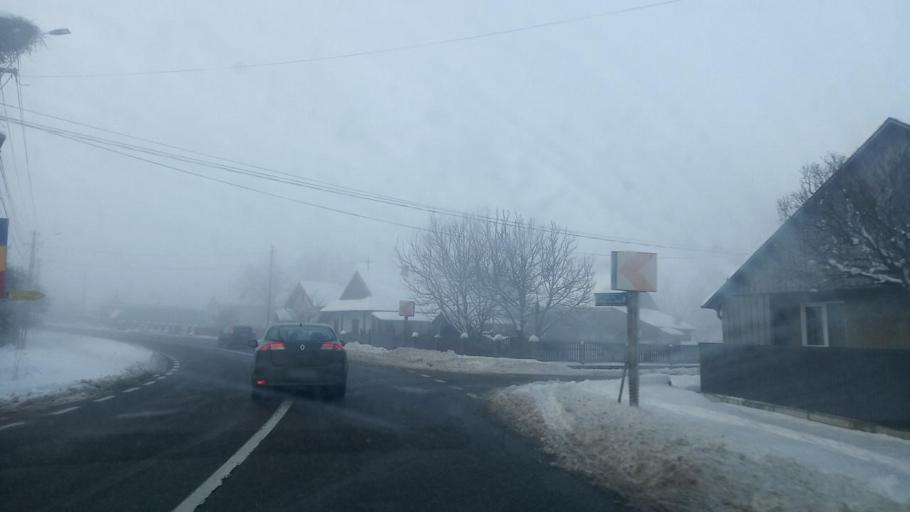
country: RO
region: Suceava
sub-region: Comuna Cornu Luncii
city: Baisesti
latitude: 47.4840
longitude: 26.0986
